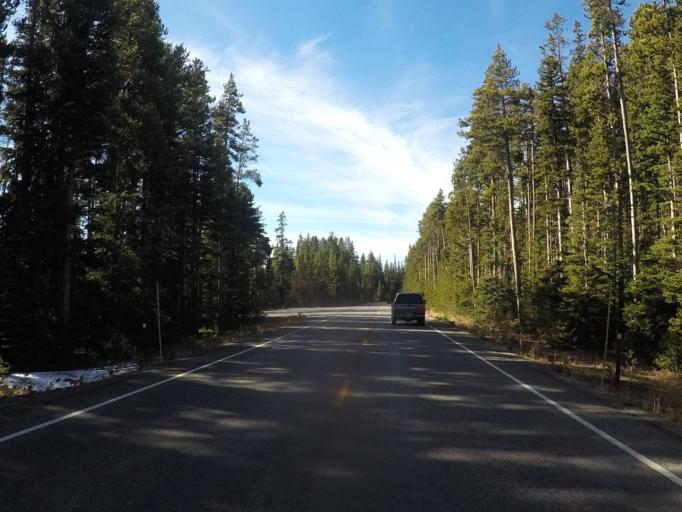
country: US
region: Montana
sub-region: Gallatin County
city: West Yellowstone
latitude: 44.4554
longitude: -110.4937
